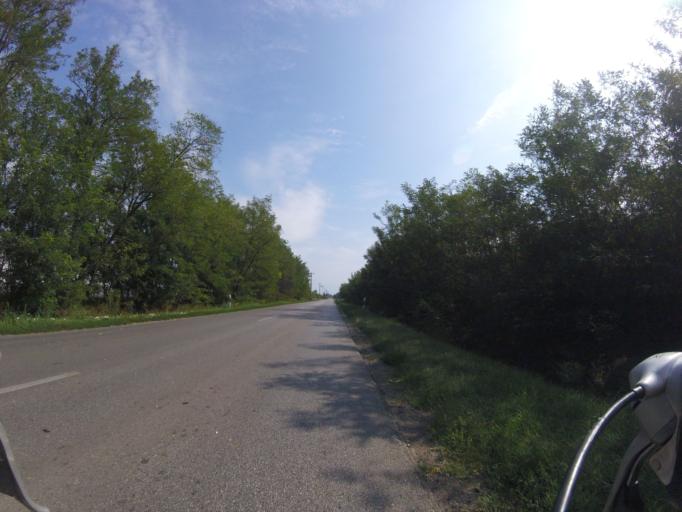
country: HU
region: Szabolcs-Szatmar-Bereg
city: Kemecse
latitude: 48.0611
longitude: 21.7874
